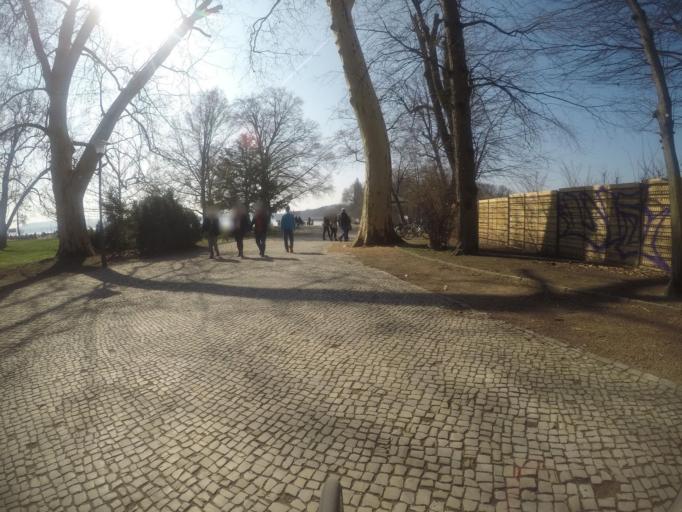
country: DE
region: Berlin
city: Friedrichshagen
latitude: 52.4452
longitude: 13.6265
